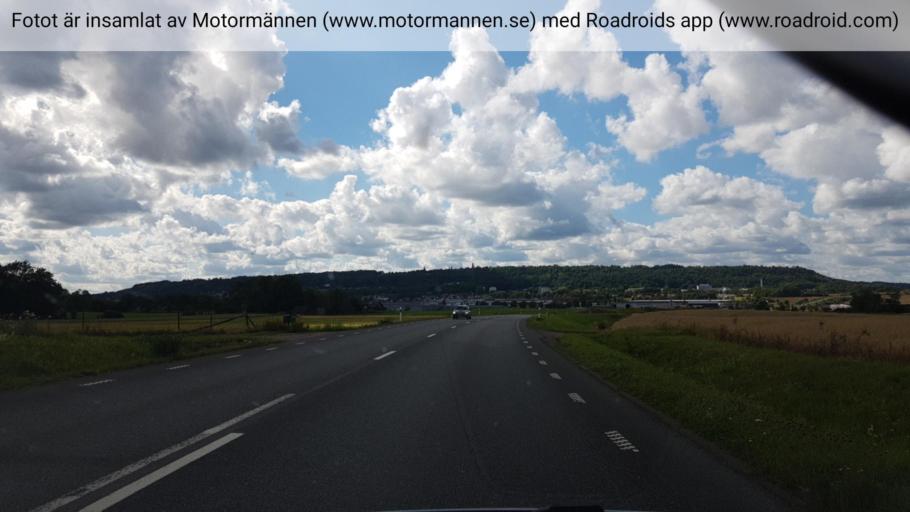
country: SE
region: Vaestra Goetaland
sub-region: Falkopings Kommun
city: Falkoeping
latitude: 58.1795
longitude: 13.5839
